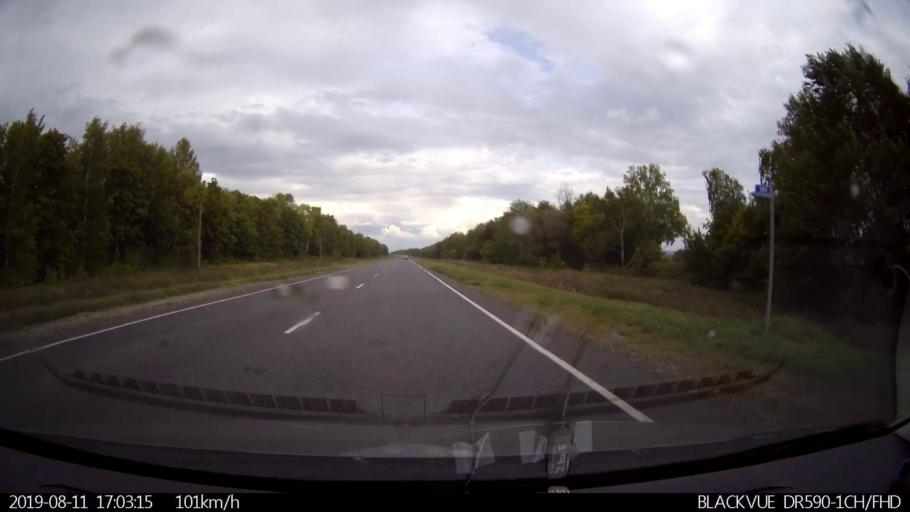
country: RU
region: Ulyanovsk
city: Mayna
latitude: 54.3036
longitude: 47.7349
